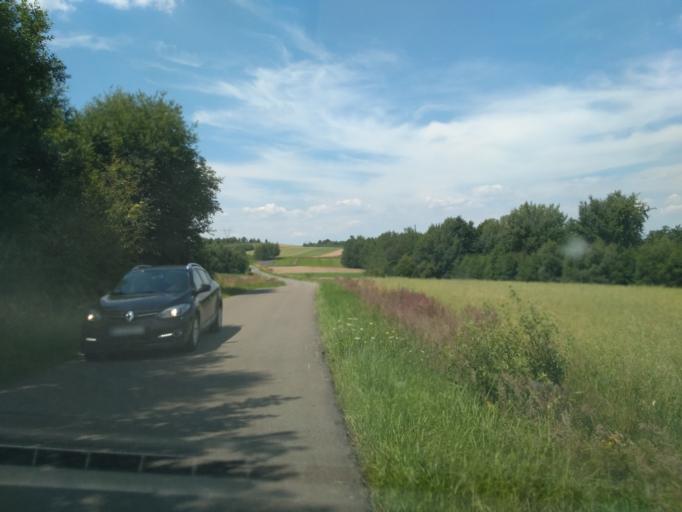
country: PL
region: Subcarpathian Voivodeship
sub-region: Powiat strzyzowski
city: Jawornik
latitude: 49.8622
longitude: 21.8743
